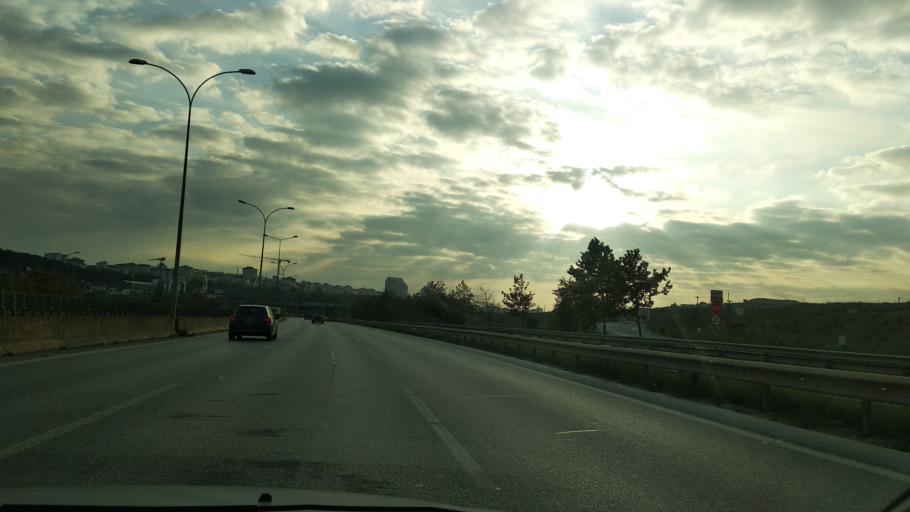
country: TR
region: Istanbul
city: Icmeler
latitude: 40.8817
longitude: 29.3173
